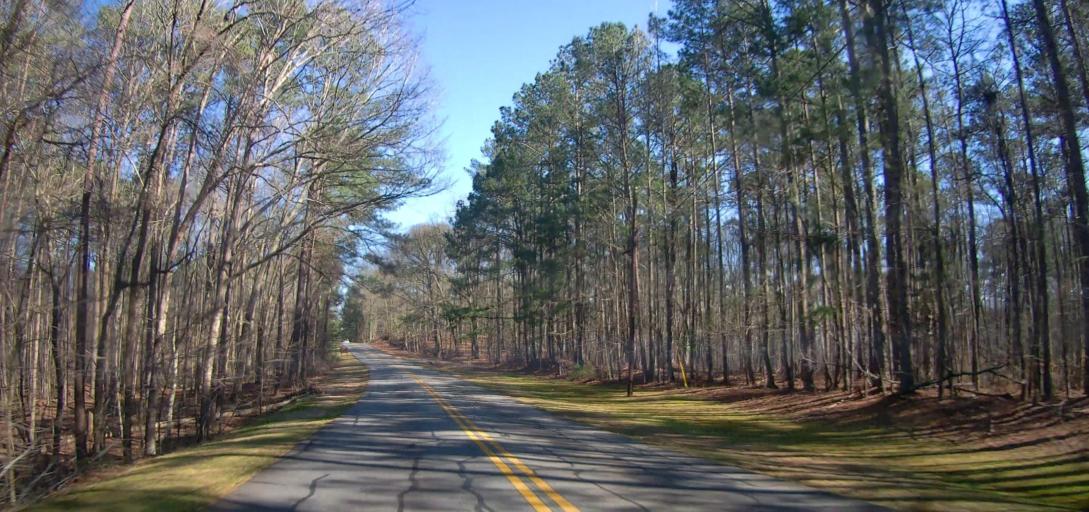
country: US
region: Georgia
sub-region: Butts County
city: Indian Springs
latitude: 33.2531
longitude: -83.9307
